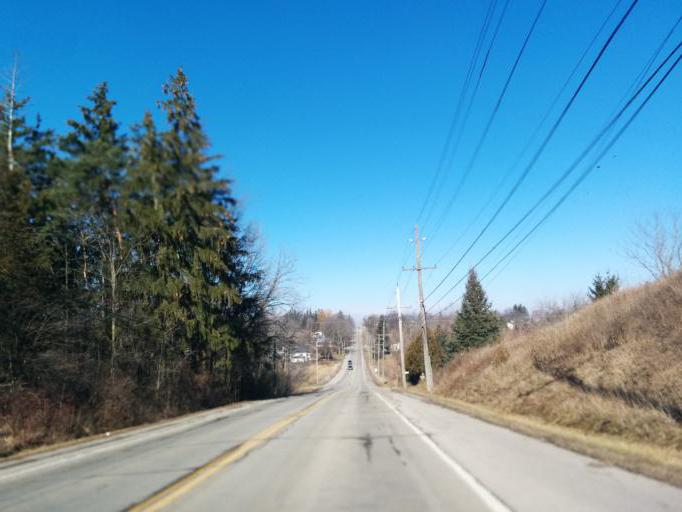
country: CA
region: Ontario
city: Brant
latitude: 43.0260
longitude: -80.3288
